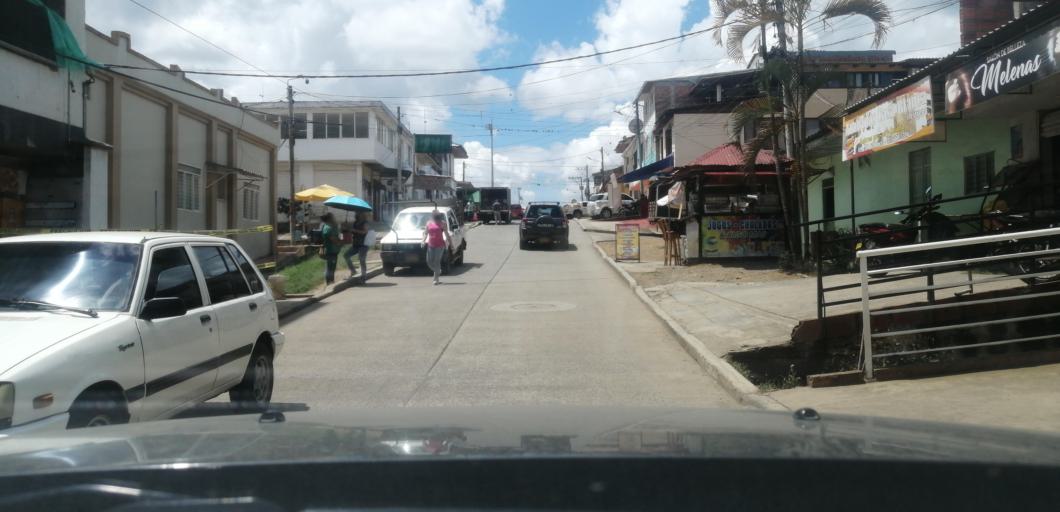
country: CO
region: Valle del Cauca
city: Restrepo
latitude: 3.8209
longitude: -76.5244
